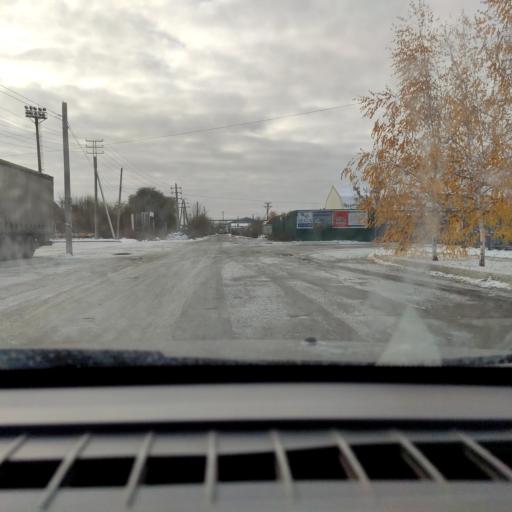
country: RU
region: Samara
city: Tol'yatti
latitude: 53.5781
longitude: 49.2843
